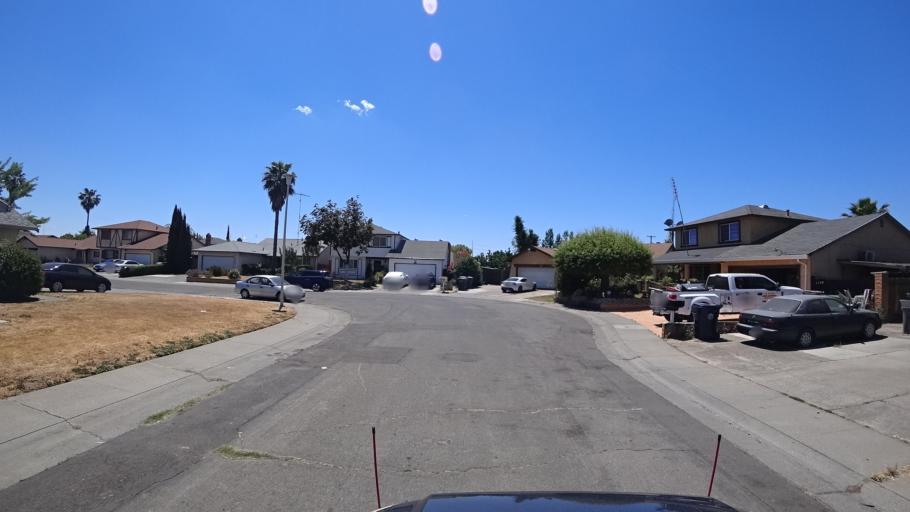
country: US
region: California
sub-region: Sacramento County
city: Florin
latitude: 38.5126
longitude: -121.4249
